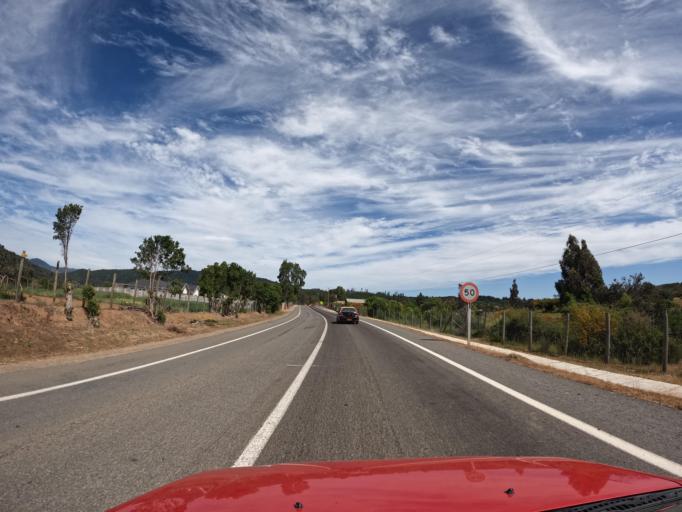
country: CL
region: Maule
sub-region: Provincia de Talca
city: Talca
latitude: -35.1256
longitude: -71.9574
